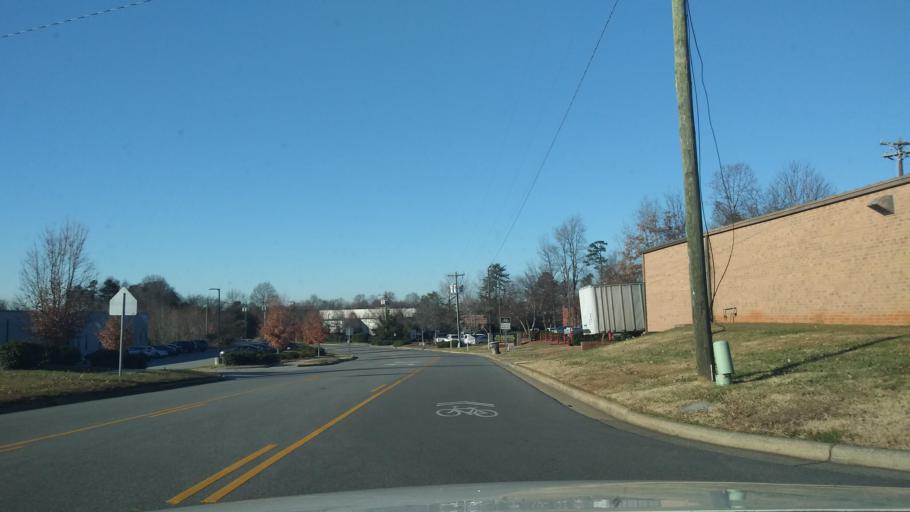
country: US
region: North Carolina
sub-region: Guilford County
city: Greensboro
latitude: 36.0276
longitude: -79.7772
